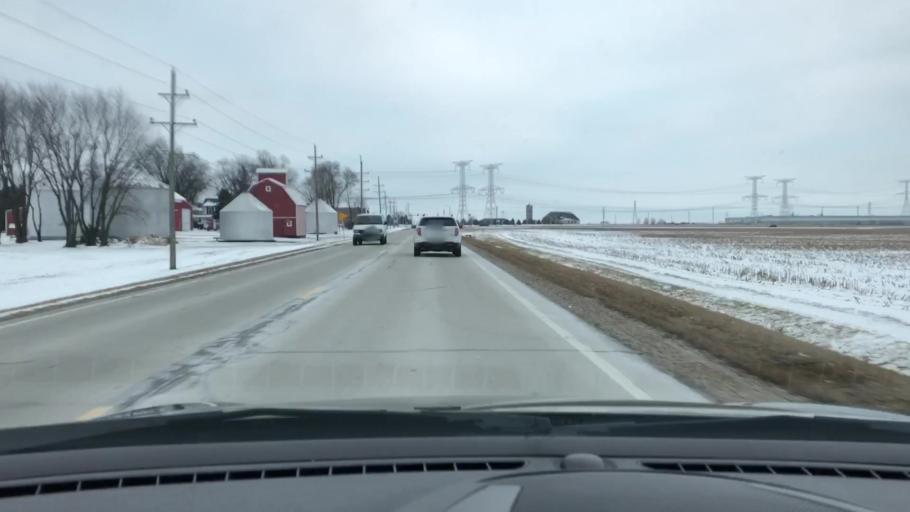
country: US
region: Illinois
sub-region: Will County
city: New Lenox
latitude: 41.5012
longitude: -88.0041
